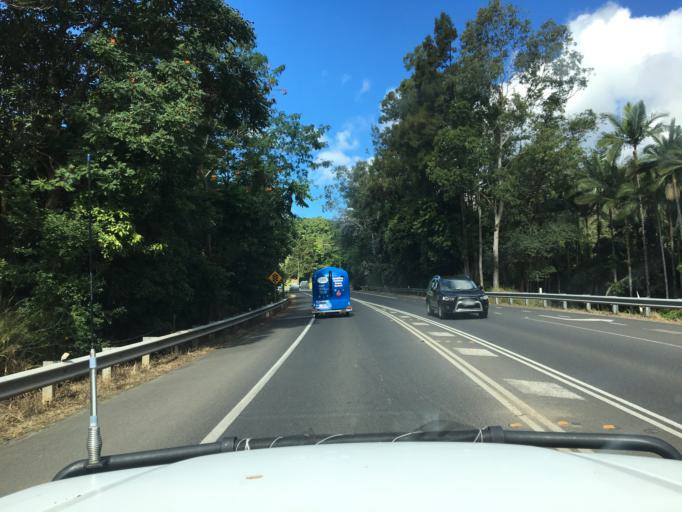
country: AU
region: Queensland
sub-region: Cairns
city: Redlynch
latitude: -16.8777
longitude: 145.6868
